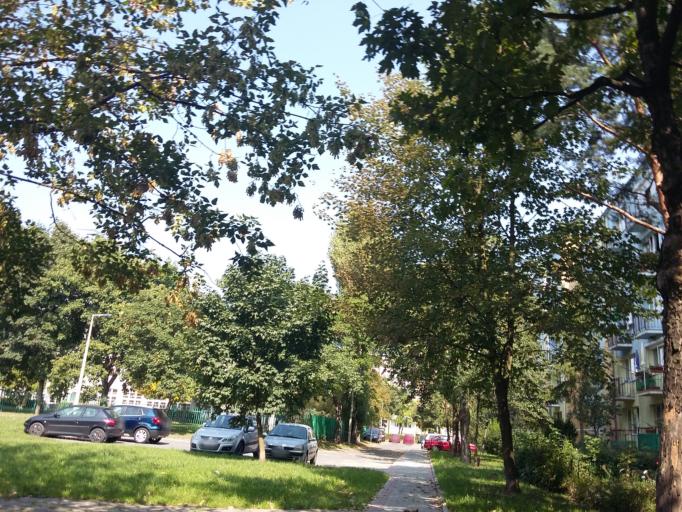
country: PL
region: Lodz Voivodeship
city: Lodz
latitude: 51.7452
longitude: 19.4149
